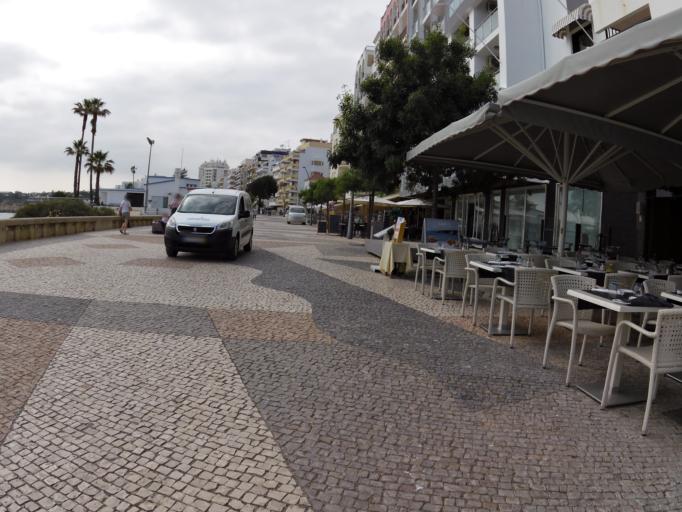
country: PT
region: Faro
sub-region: Silves
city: Armacao de Pera
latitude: 37.1013
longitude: -8.3625
